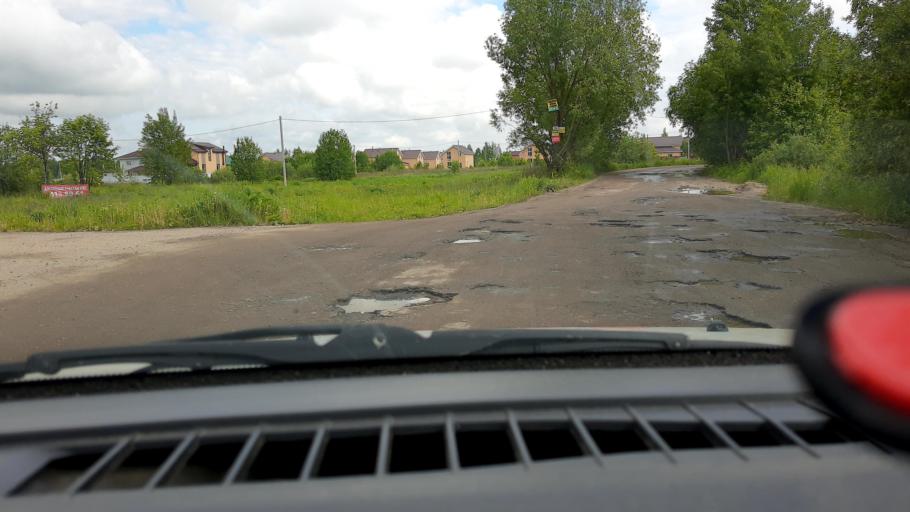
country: RU
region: Nizjnij Novgorod
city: Neklyudovo
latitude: 56.4221
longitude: 43.9563
